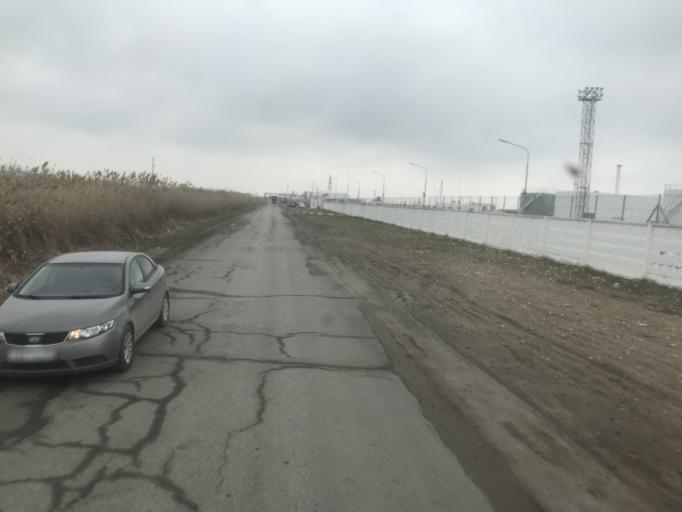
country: RU
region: Volgograd
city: Svetlyy Yar
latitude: 48.5109
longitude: 44.6383
